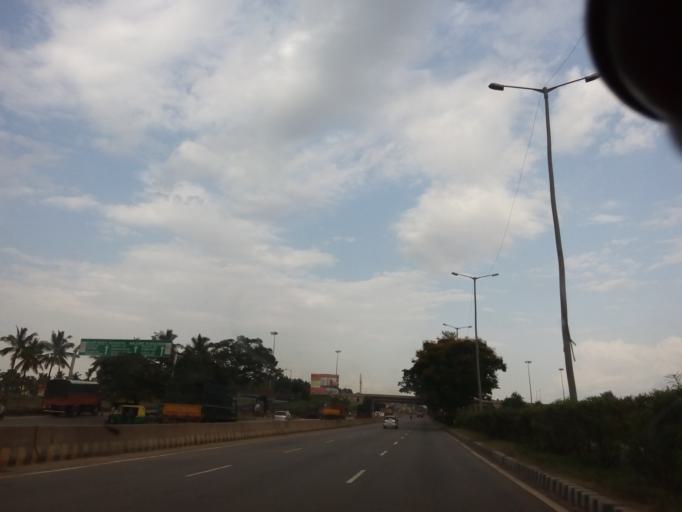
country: IN
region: Karnataka
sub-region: Bangalore Rural
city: Nelamangala
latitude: 13.0567
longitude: 77.4739
